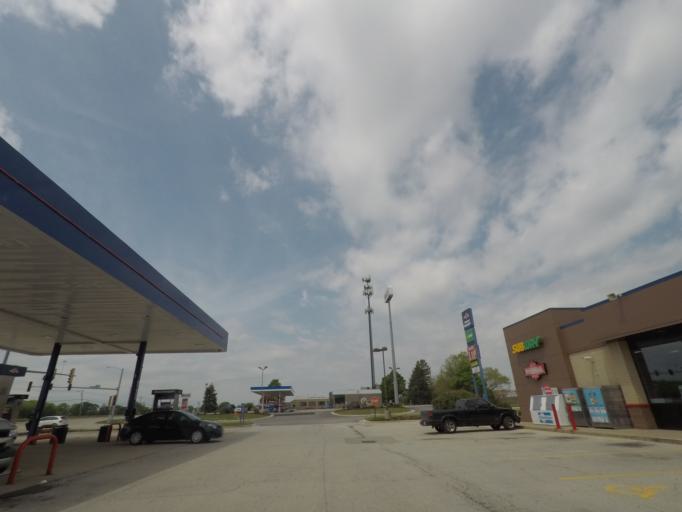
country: US
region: Illinois
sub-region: Winnebago County
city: Machesney Park
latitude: 42.3196
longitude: -88.9694
